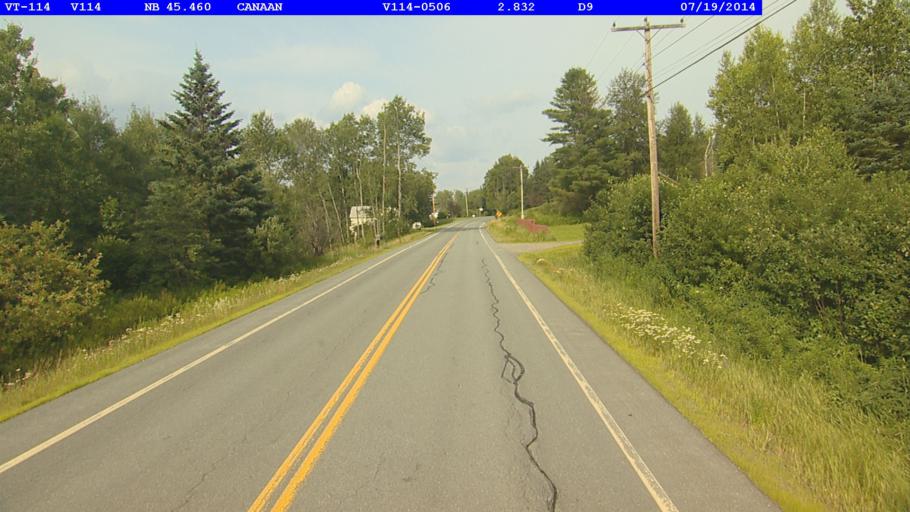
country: US
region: New Hampshire
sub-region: Coos County
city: Colebrook
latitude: 45.0072
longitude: -71.6365
